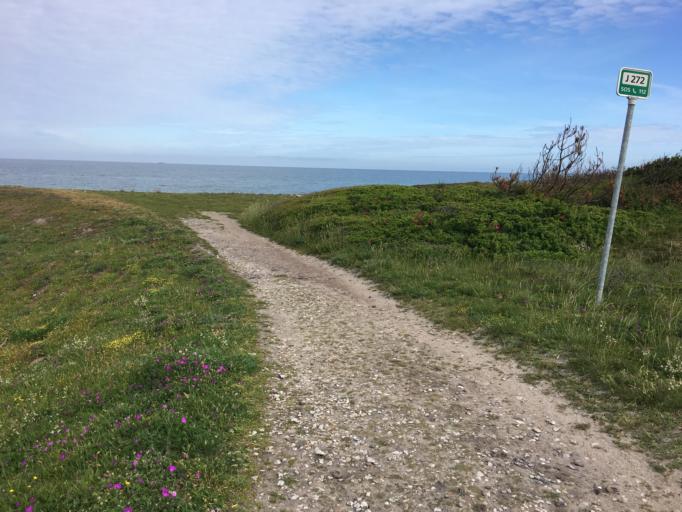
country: DK
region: Zealand
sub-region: Odsherred Kommune
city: Nykobing Sjaelland
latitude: 55.9666
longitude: 11.7456
